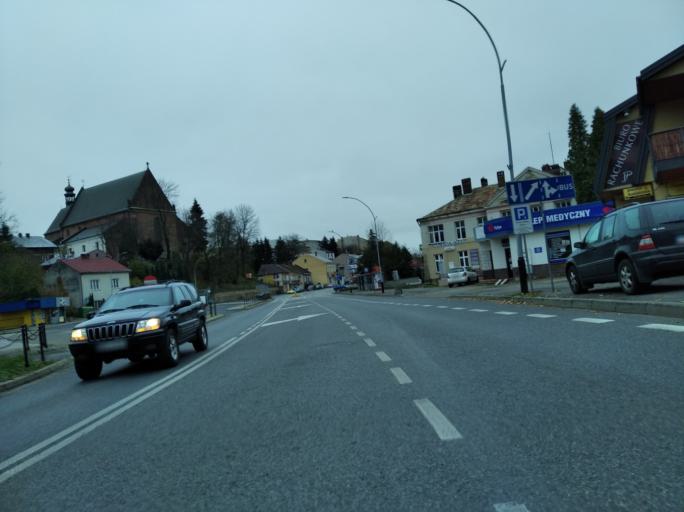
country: PL
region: Subcarpathian Voivodeship
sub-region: Krosno
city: Krosno
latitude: 49.6952
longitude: 21.7615
